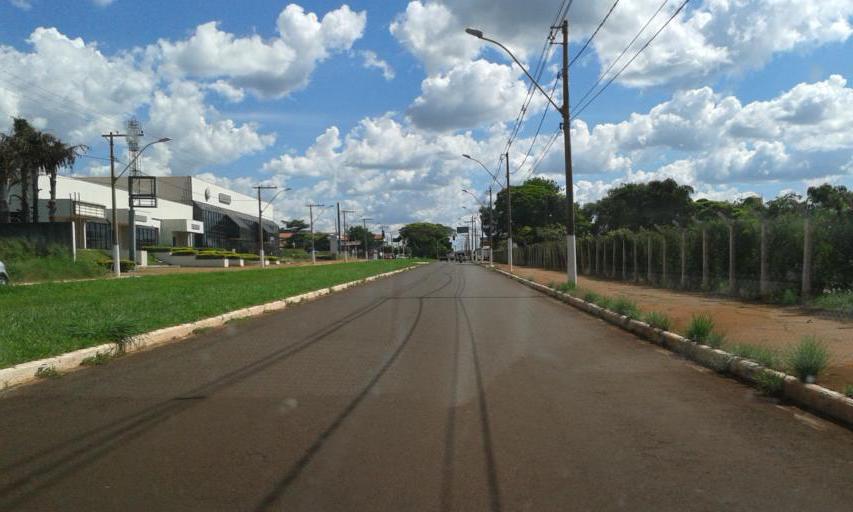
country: BR
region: Minas Gerais
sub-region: Ituiutaba
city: Ituiutaba
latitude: -18.9740
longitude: -49.4824
